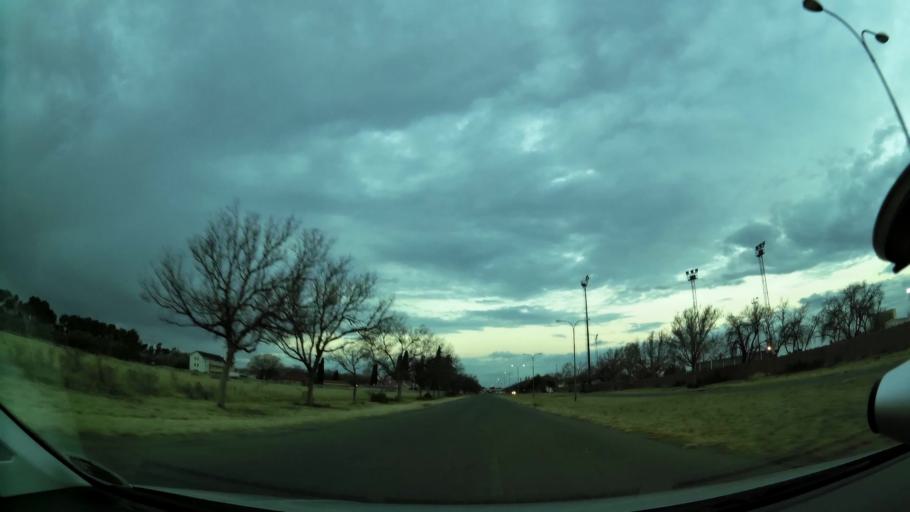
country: ZA
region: Orange Free State
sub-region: Lejweleputswa District Municipality
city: Welkom
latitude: -27.9770
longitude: 26.7522
